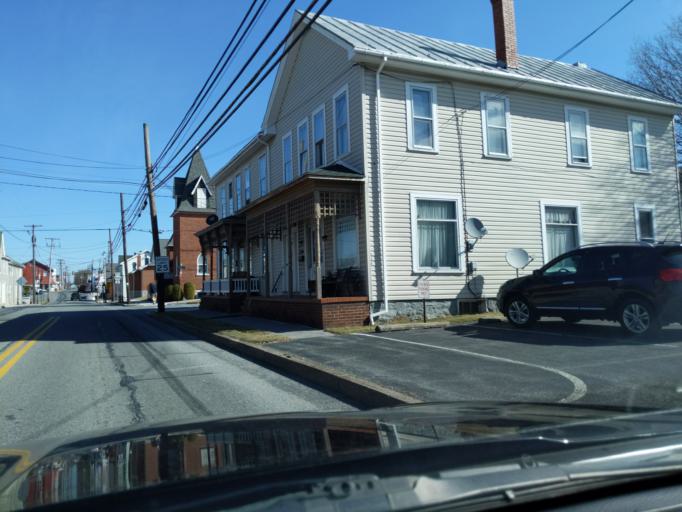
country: US
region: Pennsylvania
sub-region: Blair County
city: Martinsburg
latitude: 40.3096
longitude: -78.3260
